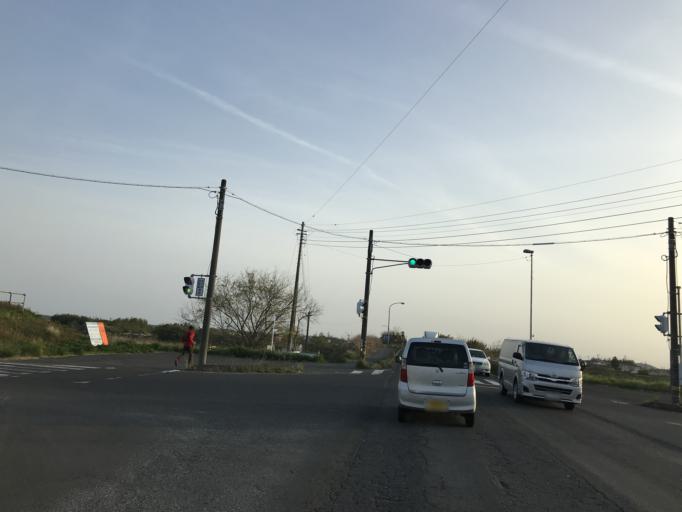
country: JP
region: Ibaraki
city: Katsuta
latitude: 36.3722
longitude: 140.5184
